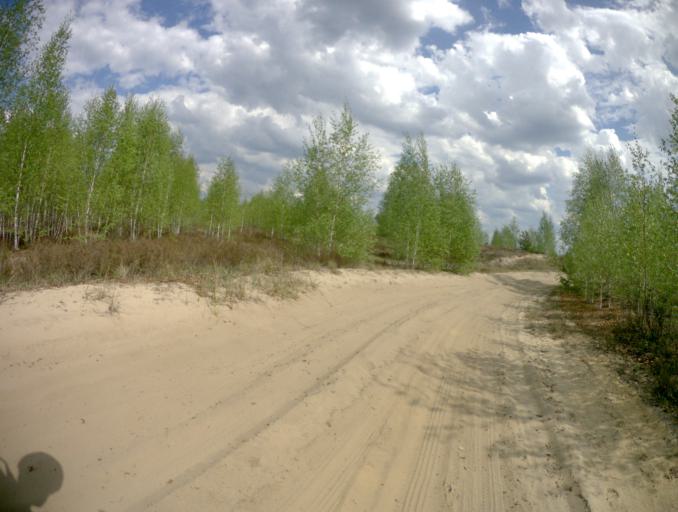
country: RU
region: Ivanovo
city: Talitsy
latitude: 56.4661
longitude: 42.2138
